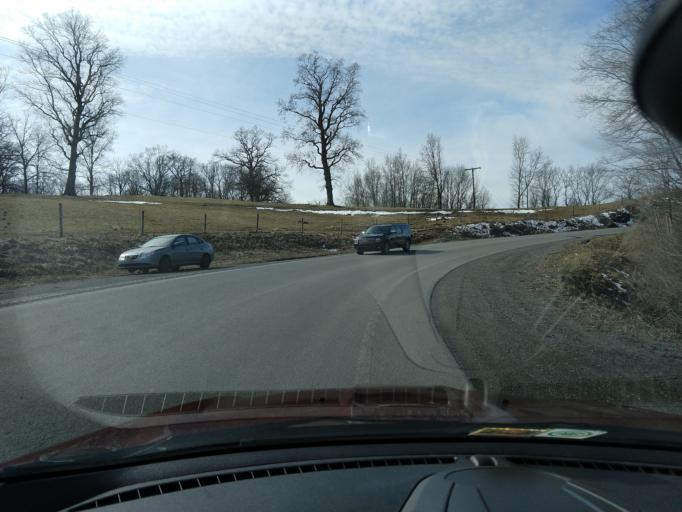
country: US
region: West Virginia
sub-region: Pocahontas County
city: Marlinton
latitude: 38.1224
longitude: -80.2372
